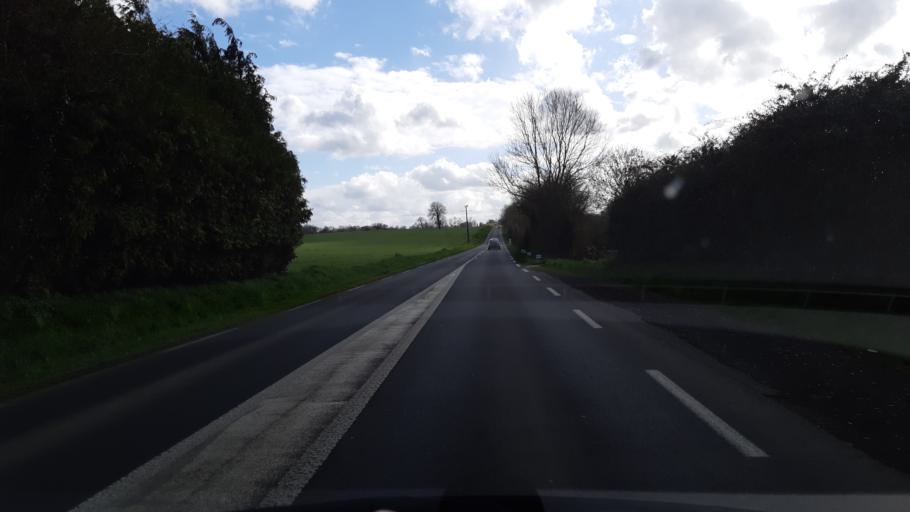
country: FR
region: Lower Normandy
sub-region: Departement de la Manche
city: Agneaux
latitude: 49.0445
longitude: -1.1285
